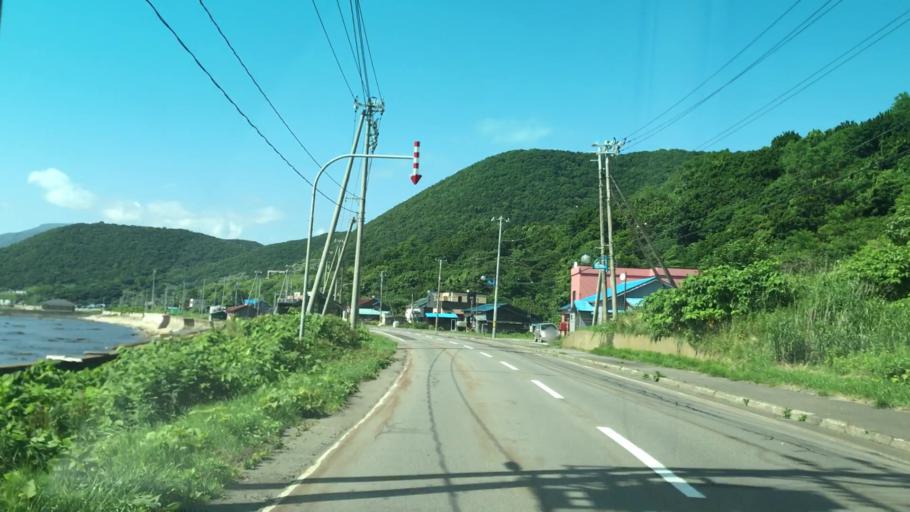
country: JP
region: Hokkaido
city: Iwanai
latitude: 43.0935
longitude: 140.4635
